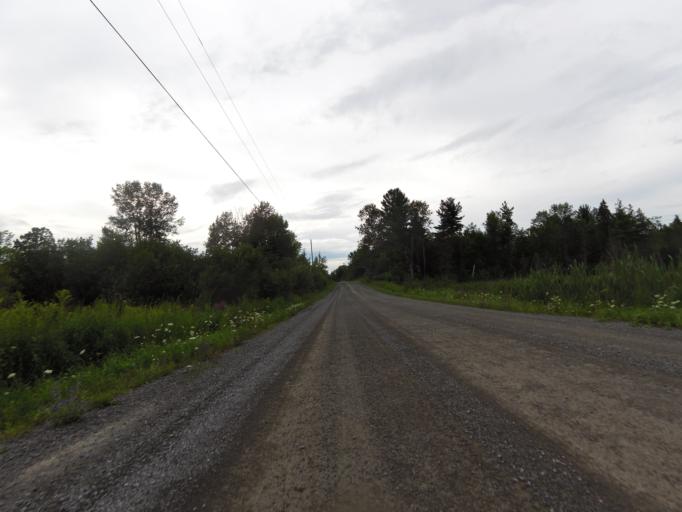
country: CA
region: Ontario
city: Carleton Place
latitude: 45.1592
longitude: -76.2672
